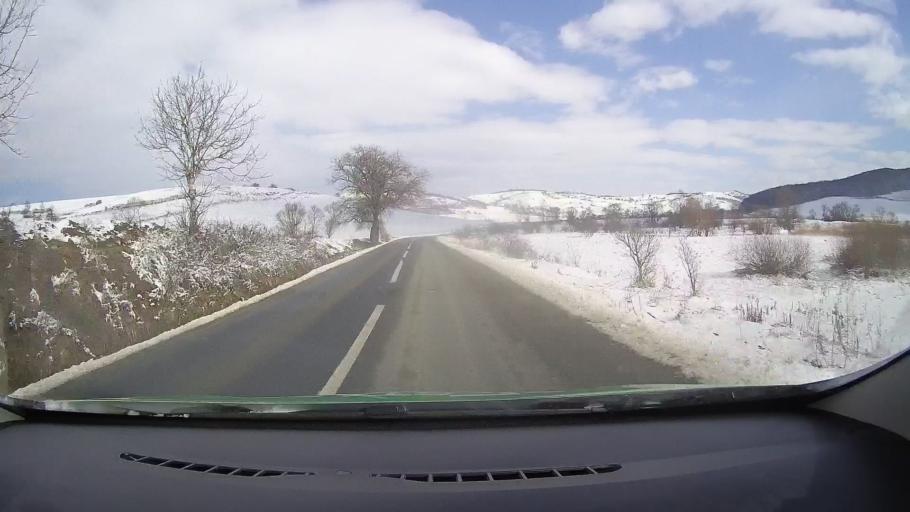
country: RO
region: Sibiu
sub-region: Comuna Altina
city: Altina
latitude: 45.9628
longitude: 24.4625
